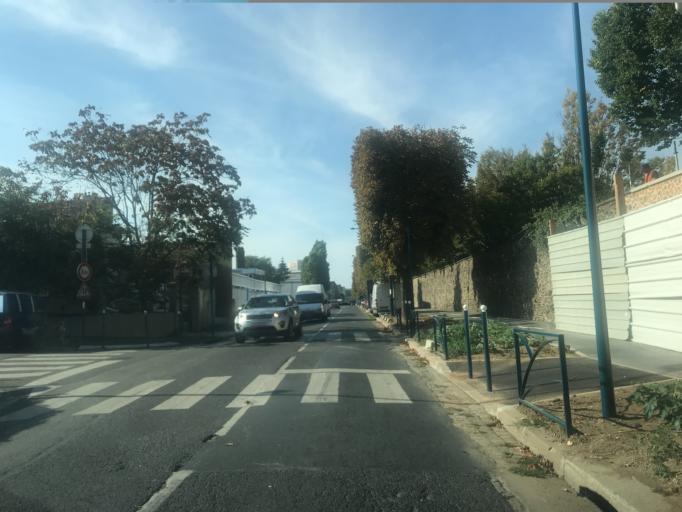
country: FR
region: Ile-de-France
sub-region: Departement de Seine-Saint-Denis
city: Pantin
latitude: 48.9034
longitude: 2.4041
